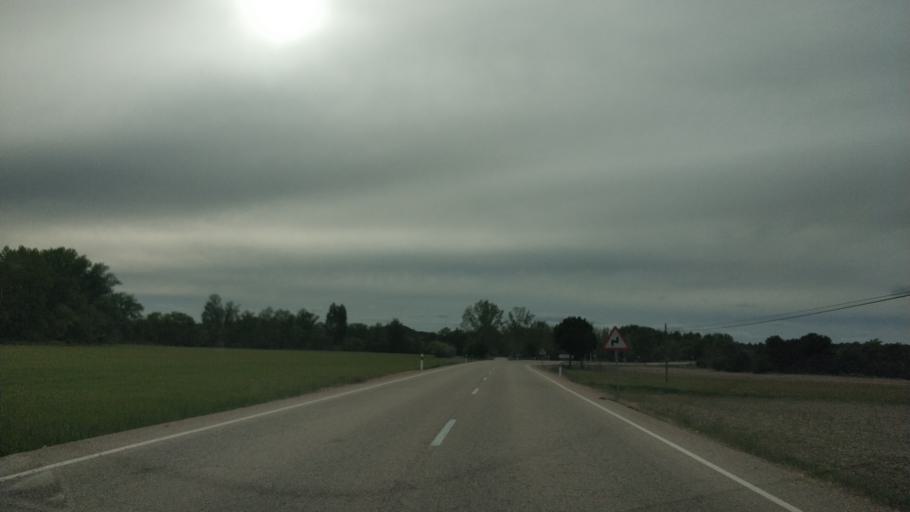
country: ES
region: Castille and Leon
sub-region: Provincia de Soria
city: Bayubas de Abajo
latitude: 41.5002
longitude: -2.8844
